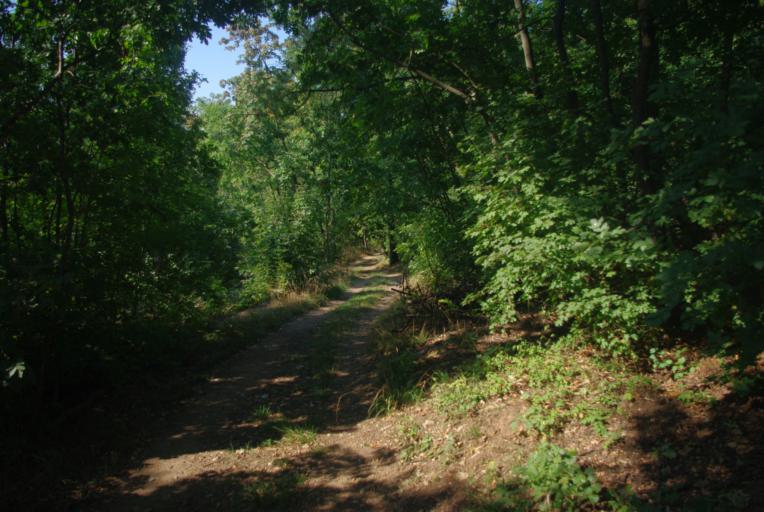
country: HU
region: Budapest
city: Budapest II. keruelet
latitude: 47.5436
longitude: 18.9821
